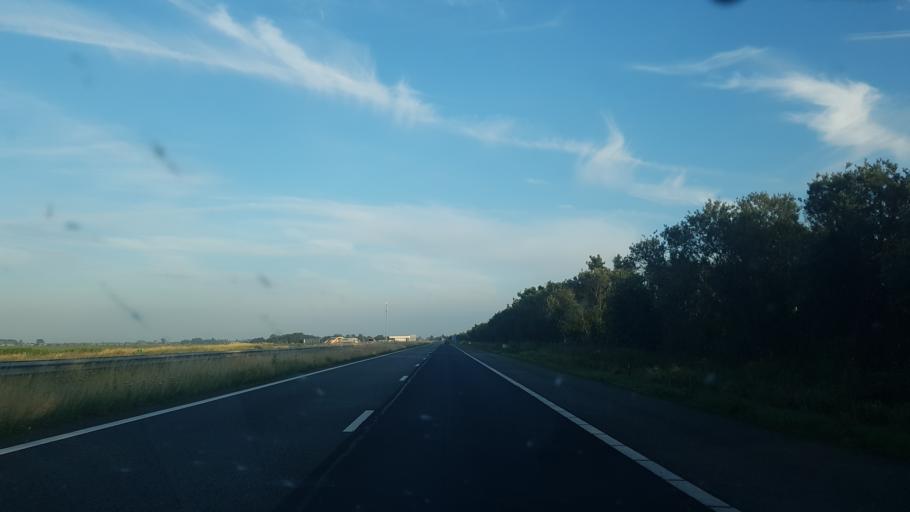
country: NL
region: Friesland
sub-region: Gemeente Leeuwarden
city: Wirdum
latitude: 53.1351
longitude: 5.8005
